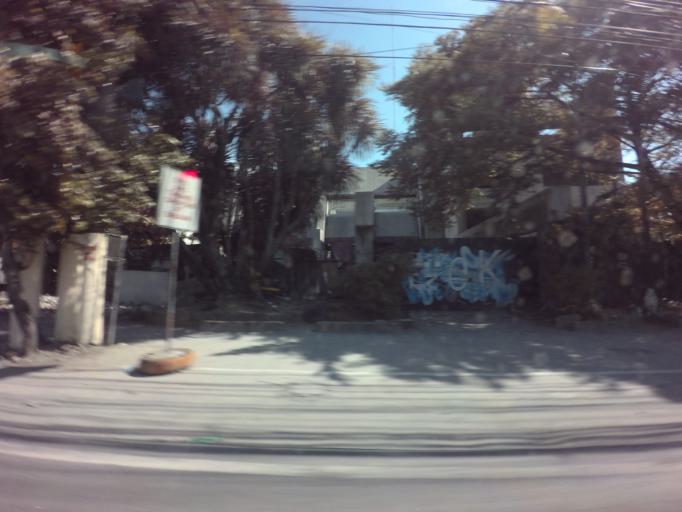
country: PH
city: Sambayanihan People's Village
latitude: 14.4441
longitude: 120.9944
